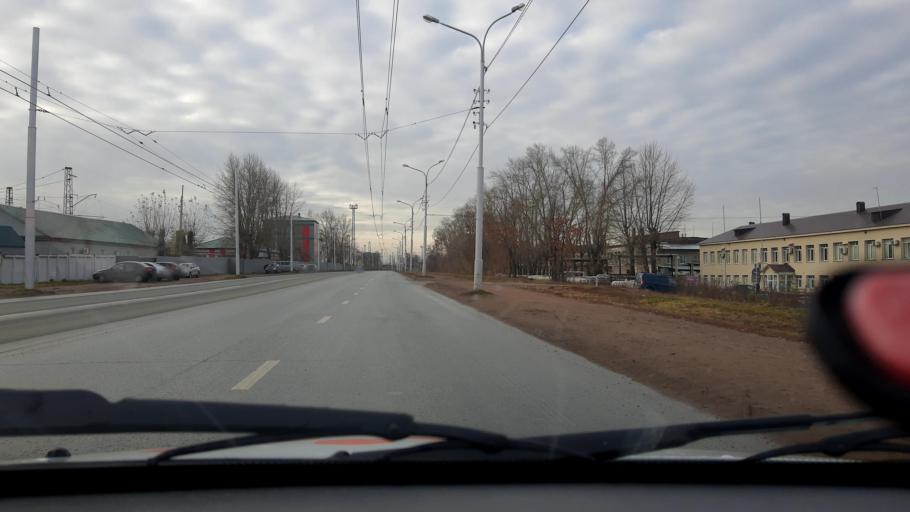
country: RU
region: Bashkortostan
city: Ufa
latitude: 54.8334
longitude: 56.0894
